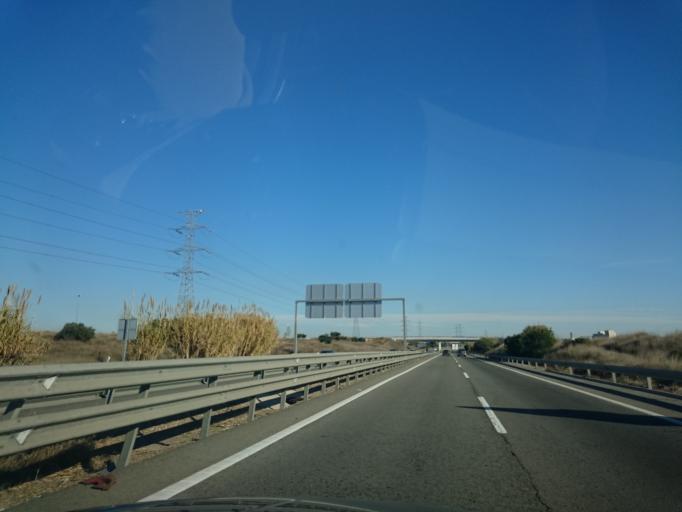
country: ES
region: Catalonia
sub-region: Provincia de Tarragona
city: Vila-seca
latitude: 41.1249
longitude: 1.1657
